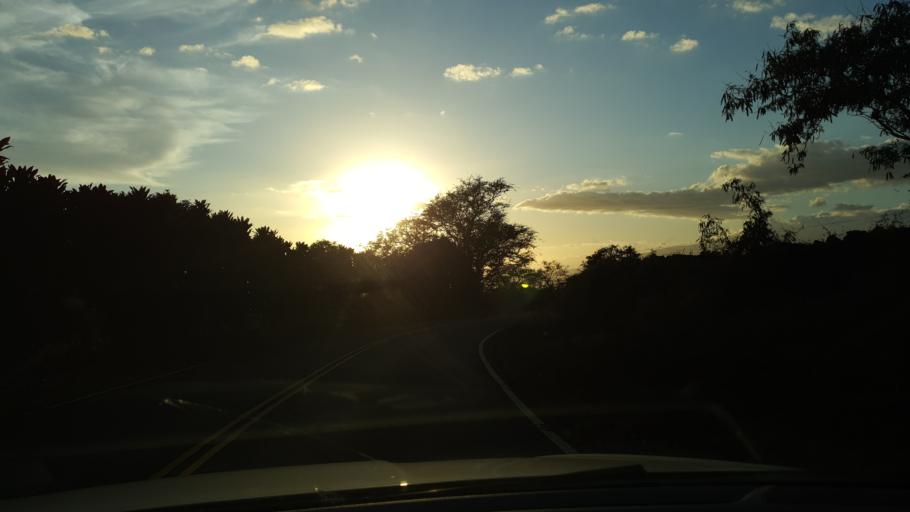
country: US
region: Hawaii
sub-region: Maui County
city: Pukalani
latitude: 20.7835
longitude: -156.3444
